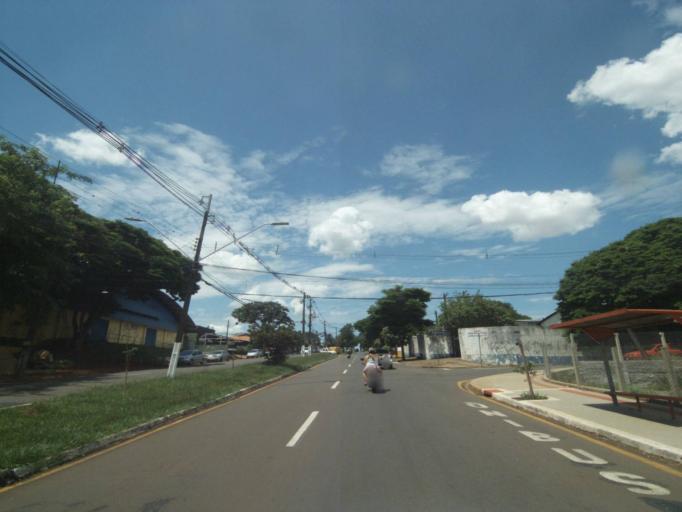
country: BR
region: Parana
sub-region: Londrina
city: Londrina
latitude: -23.3099
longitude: -51.2037
